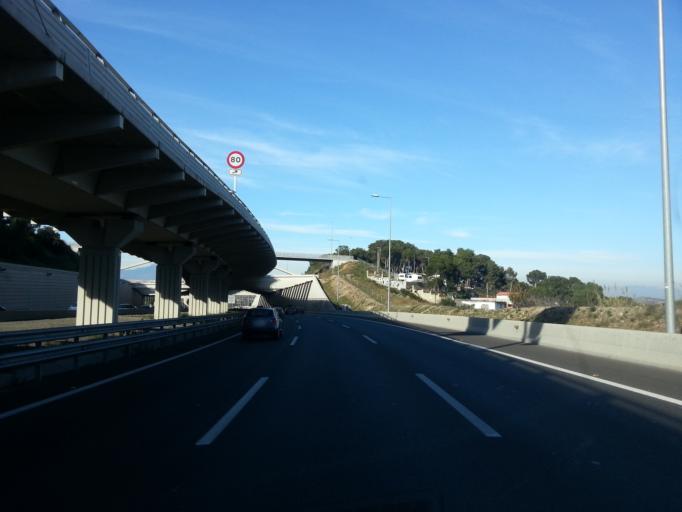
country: ES
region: Catalonia
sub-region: Provincia de Barcelona
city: Ripollet
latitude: 41.4773
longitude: 2.1629
